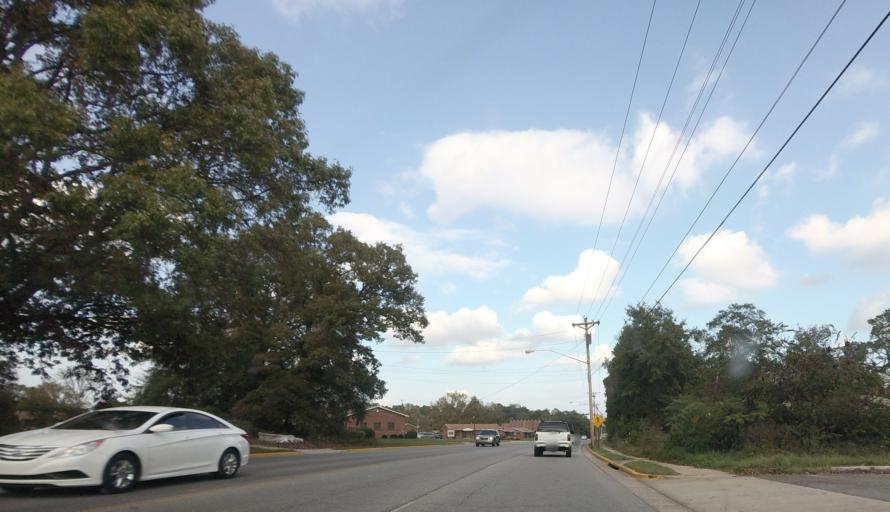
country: US
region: Georgia
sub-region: Houston County
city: Warner Robins
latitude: 32.6271
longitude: -83.6194
